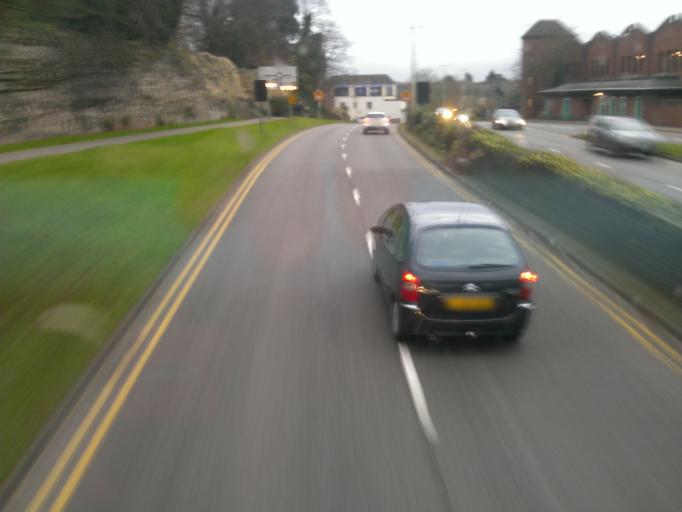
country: GB
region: England
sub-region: Essex
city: Colchester
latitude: 51.8894
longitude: 0.8937
